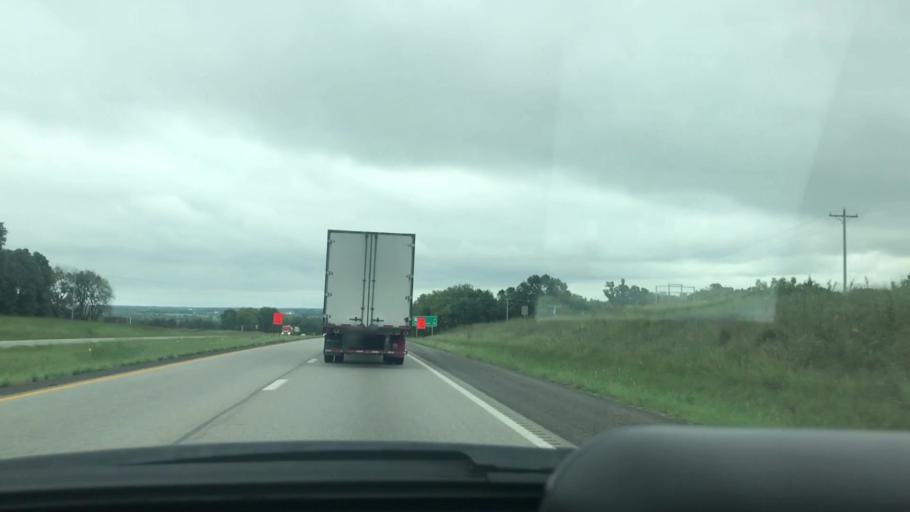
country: US
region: Missouri
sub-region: Greene County
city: Republic
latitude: 37.1858
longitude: -93.5534
